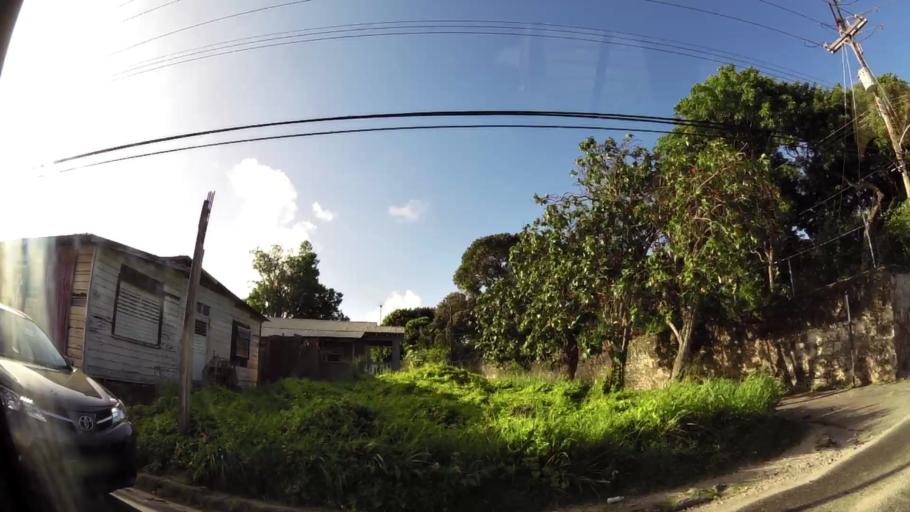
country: BB
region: Saint Michael
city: Bridgetown
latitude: 13.0860
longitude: -59.5973
